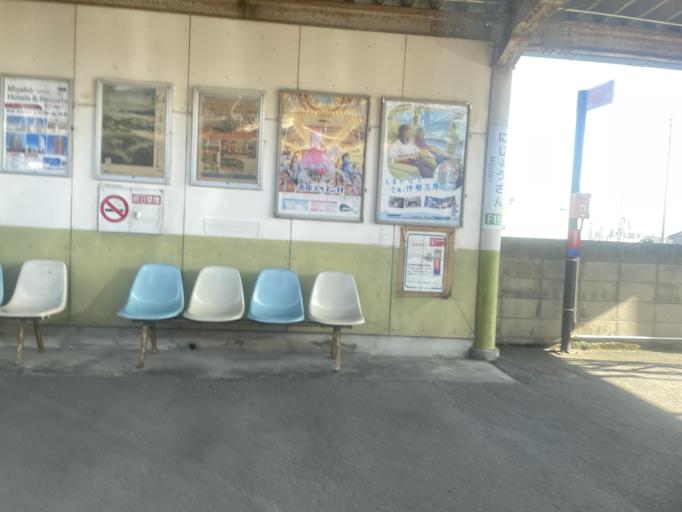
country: JP
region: Osaka
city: Kashihara
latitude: 34.5389
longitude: 135.6863
